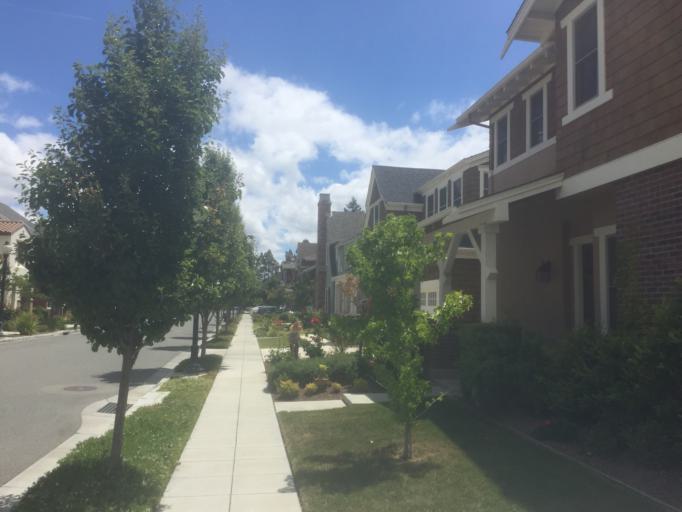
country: US
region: California
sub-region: Santa Clara County
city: Mountain View
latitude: 37.3835
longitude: -122.0891
